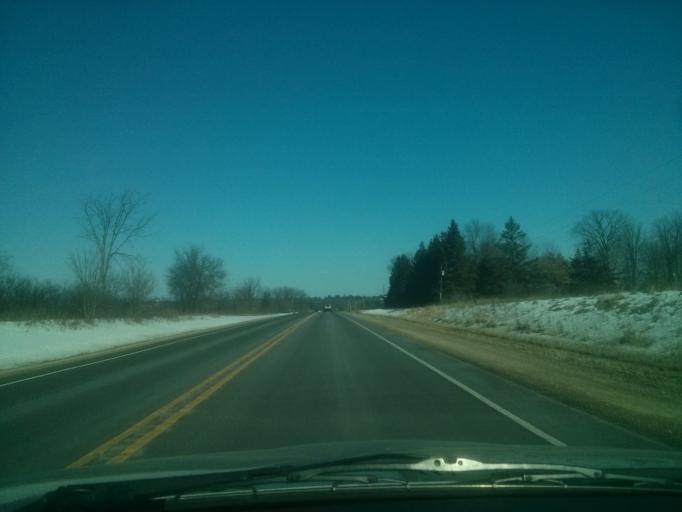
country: US
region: Wisconsin
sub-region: Polk County
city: Clear Lake
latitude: 45.1601
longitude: -92.2824
